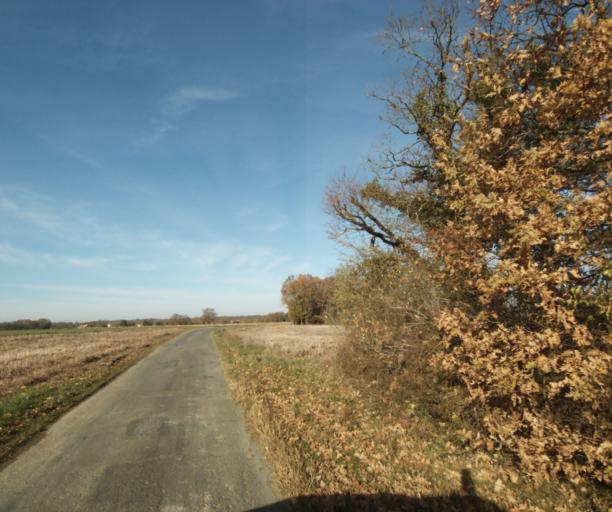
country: FR
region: Poitou-Charentes
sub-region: Departement de la Charente-Maritime
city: Ecoyeux
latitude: 45.7556
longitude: -0.4933
